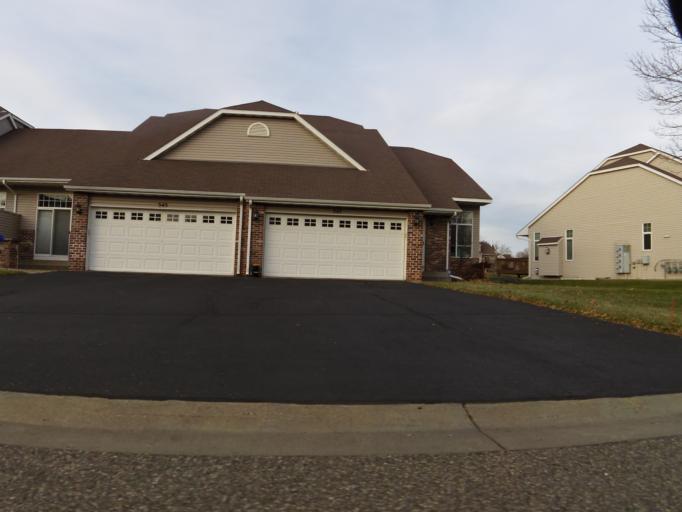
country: US
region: Wisconsin
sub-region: Saint Croix County
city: Hudson
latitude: 44.9760
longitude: -92.7340
